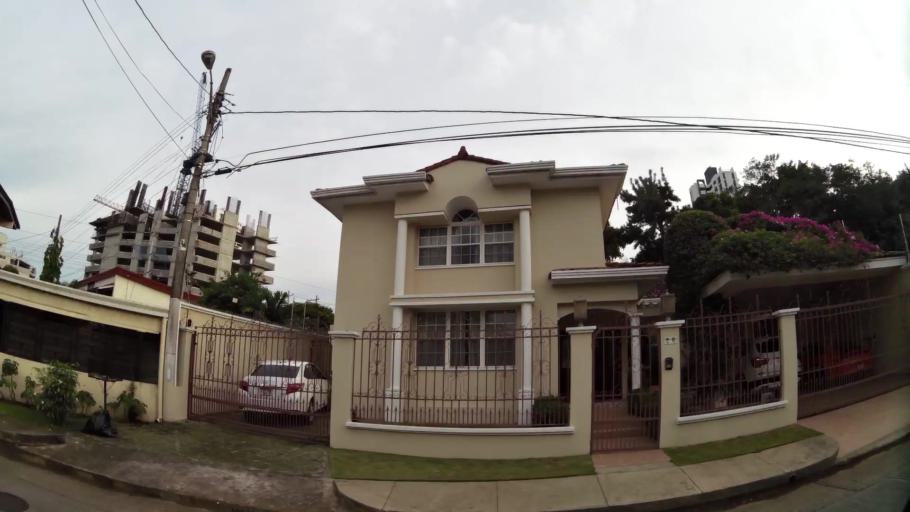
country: PA
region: Panama
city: Panama
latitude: 8.9962
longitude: -79.4996
